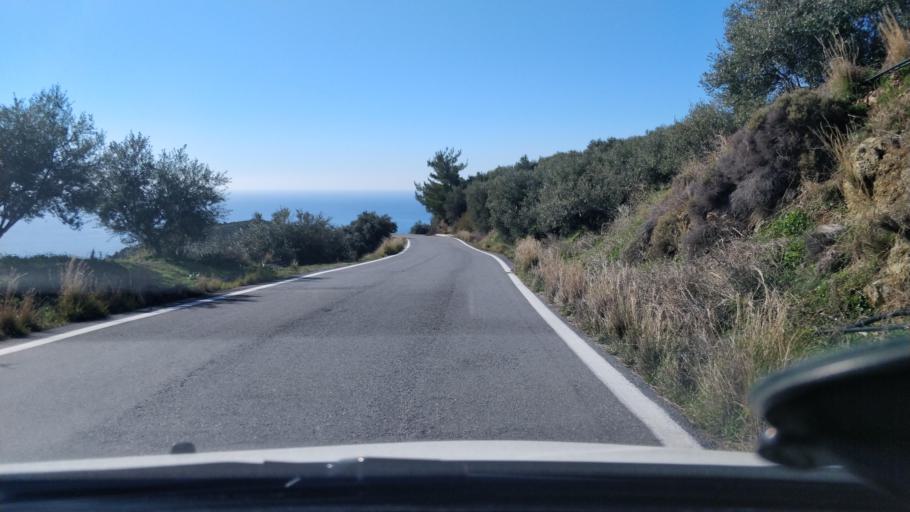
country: GR
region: Crete
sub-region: Nomos Irakleiou
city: Arkalochori
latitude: 35.0115
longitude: 25.4451
